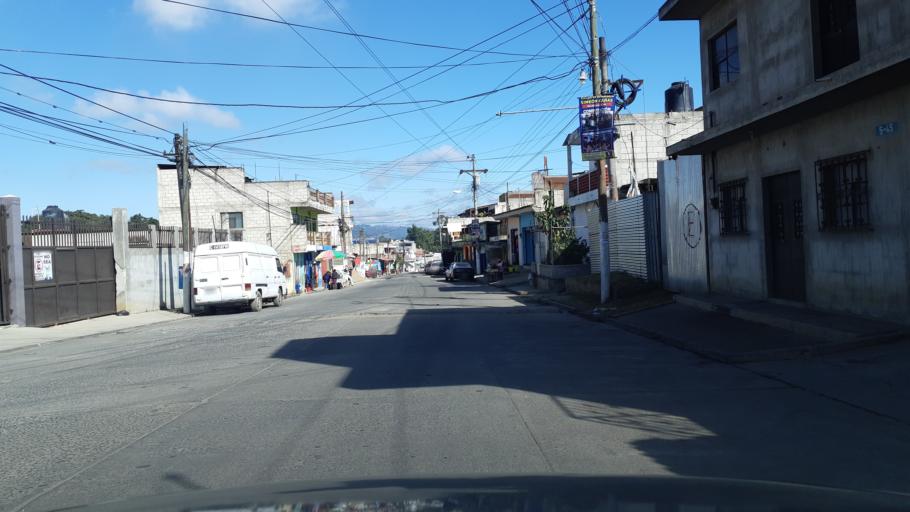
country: GT
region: Chimaltenango
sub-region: Municipio de Chimaltenango
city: Chimaltenango
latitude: 14.6556
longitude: -90.8219
